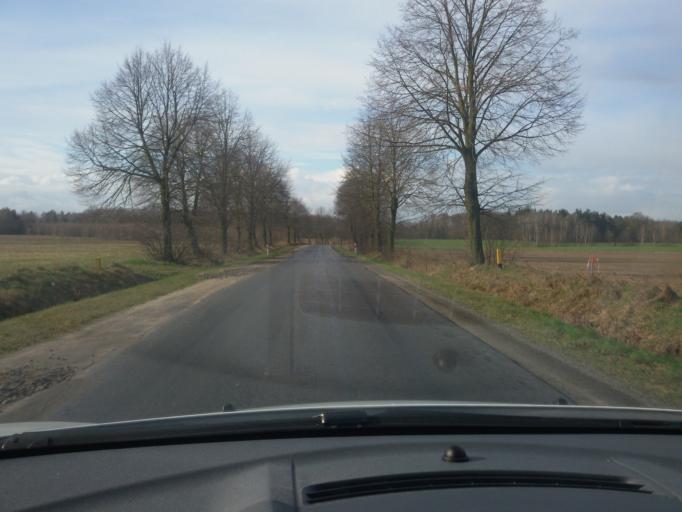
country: PL
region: Lubusz
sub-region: Powiat nowosolski
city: Nowe Miasteczko
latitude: 51.7072
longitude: 15.7487
